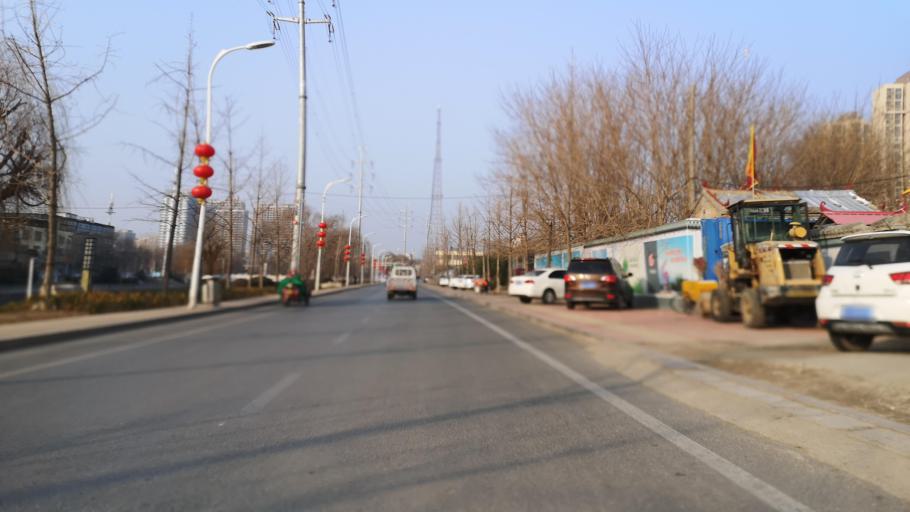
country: CN
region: Henan Sheng
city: Zhongyuanlu
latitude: 35.7735
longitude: 115.0486
